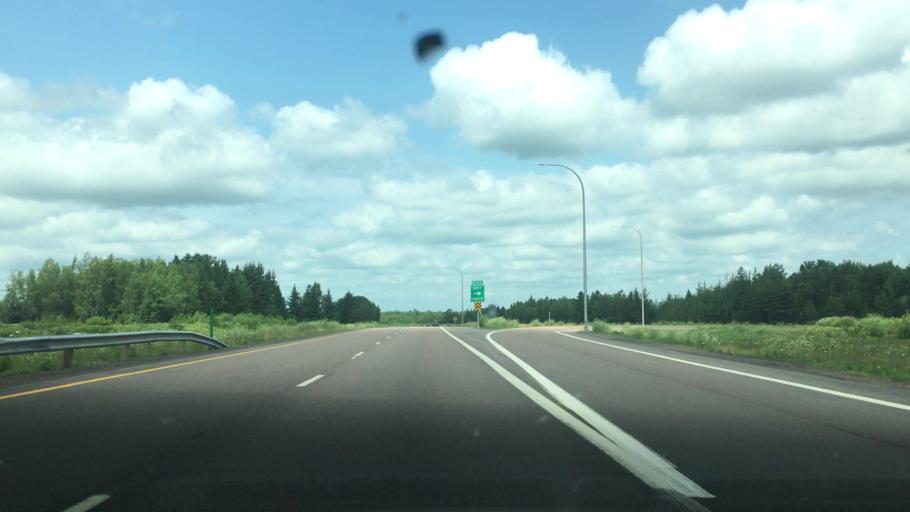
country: CA
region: New Brunswick
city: Dieppe
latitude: 46.1011
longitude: -64.6064
